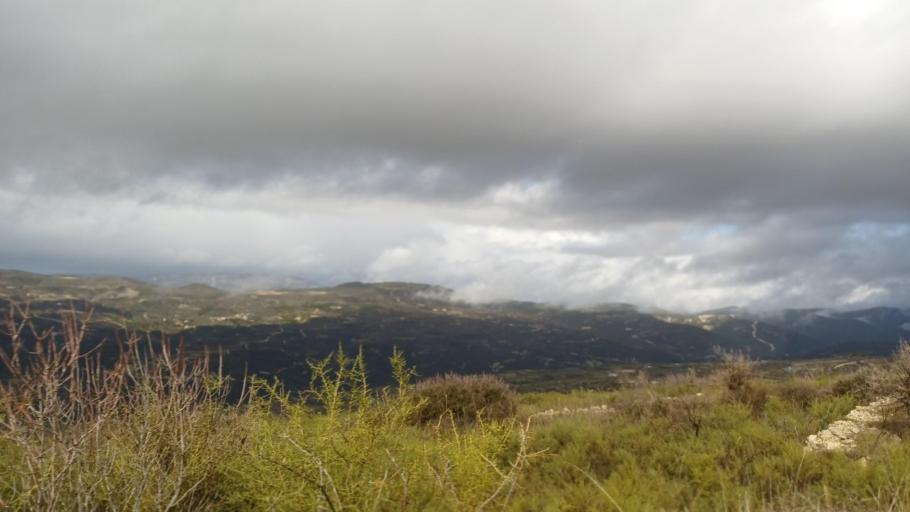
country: CY
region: Limassol
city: Pachna
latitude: 34.8263
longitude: 32.7393
